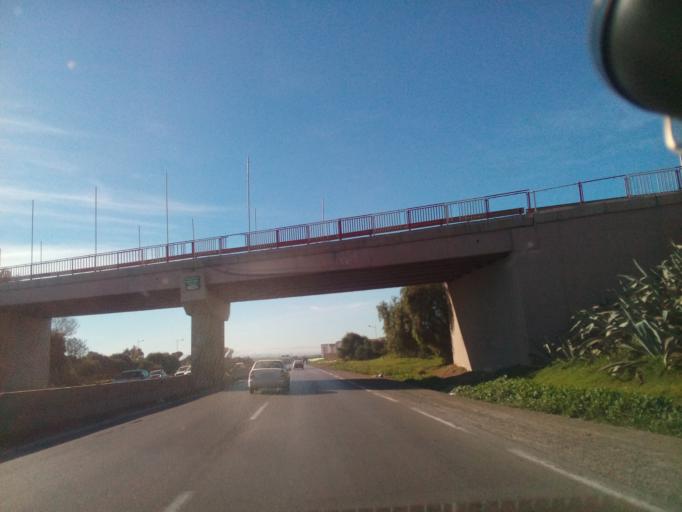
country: DZ
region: Oran
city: Ain el Bya
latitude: 35.7858
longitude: -0.4111
